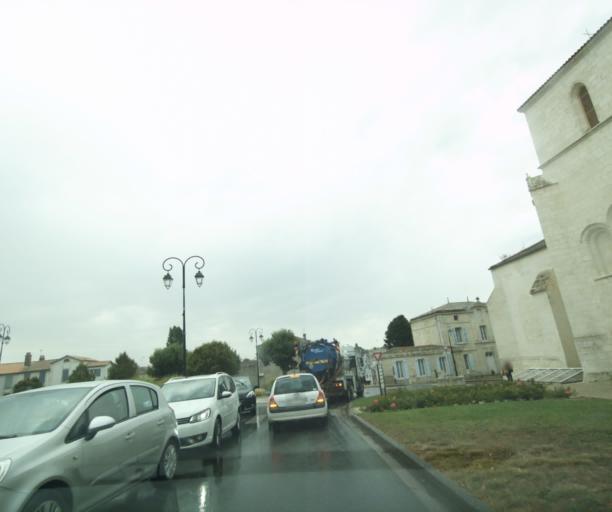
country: FR
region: Poitou-Charentes
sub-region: Departement de la Charente-Maritime
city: Tonnay-Charente
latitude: 45.9444
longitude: -0.8933
